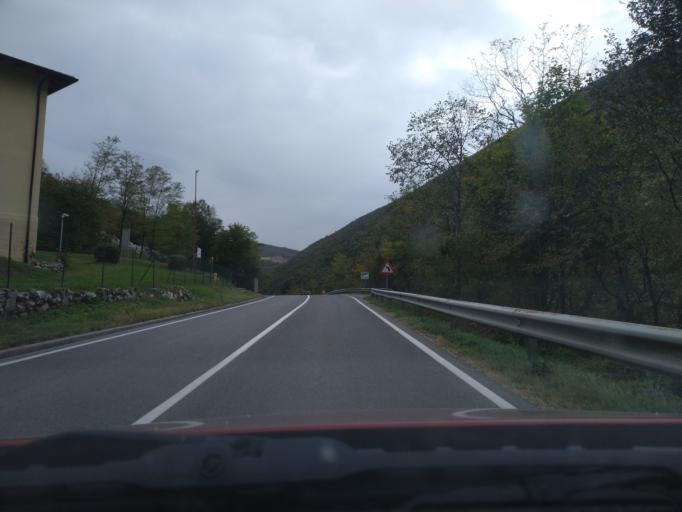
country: SI
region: Nova Gorica
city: Solkan
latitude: 45.9925
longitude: 13.6427
